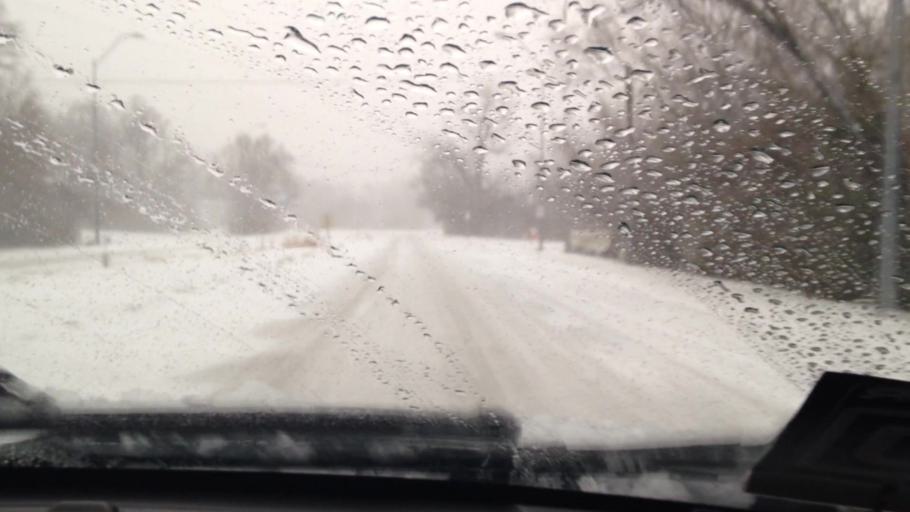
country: US
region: Missouri
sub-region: Jackson County
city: Raytown
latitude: 39.0342
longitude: -94.4737
